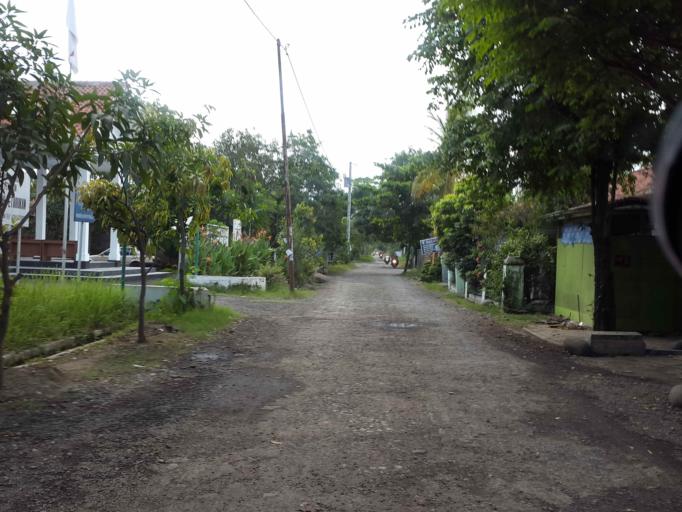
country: ID
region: Central Java
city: Petarukan
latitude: -6.8928
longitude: 109.4585
